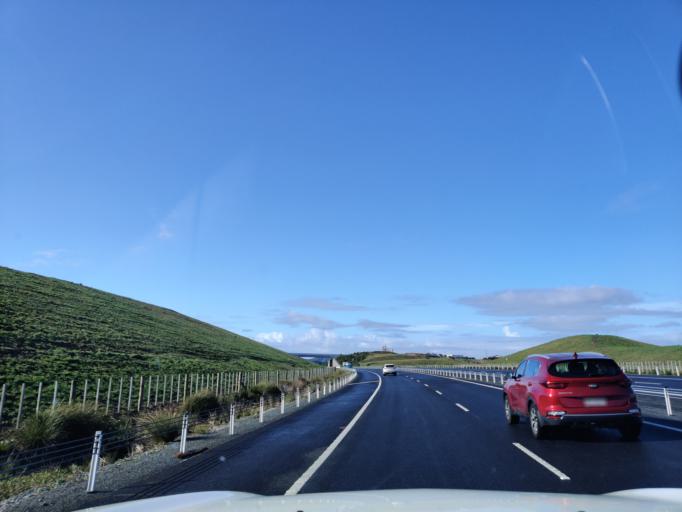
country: NZ
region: Waikato
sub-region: Waikato District
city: Te Kauwhata
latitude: -37.5201
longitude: 175.1728
